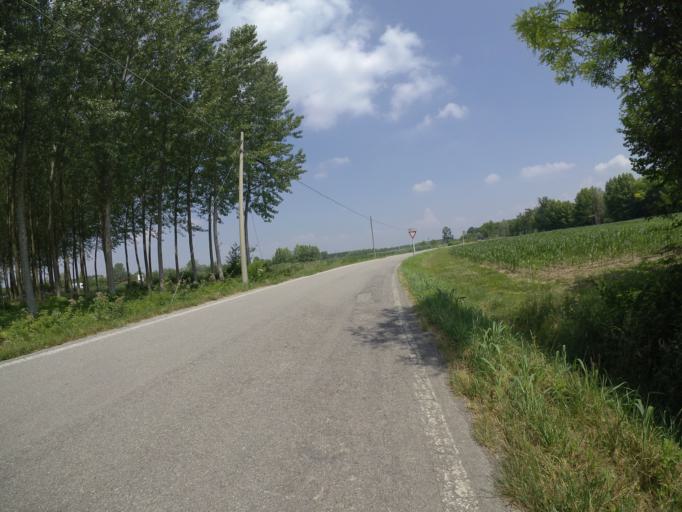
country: IT
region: Friuli Venezia Giulia
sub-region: Provincia di Udine
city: Bertiolo
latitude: 45.9117
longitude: 13.0472
